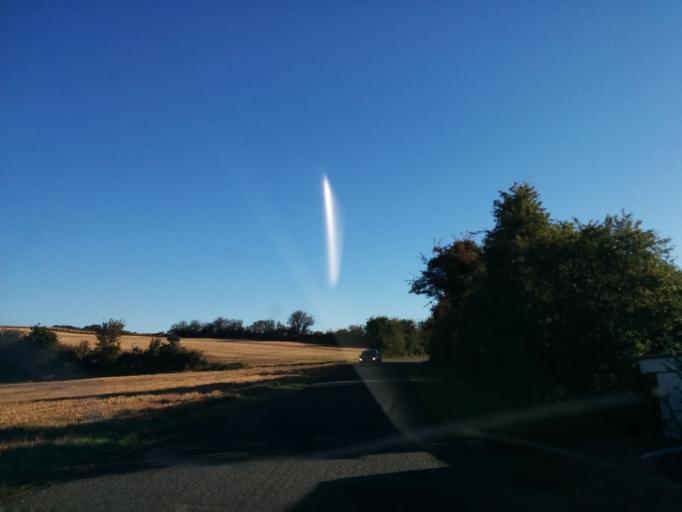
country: DK
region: South Denmark
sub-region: Kolding Kommune
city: Sonder Bjert
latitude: 55.4042
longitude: 9.5580
